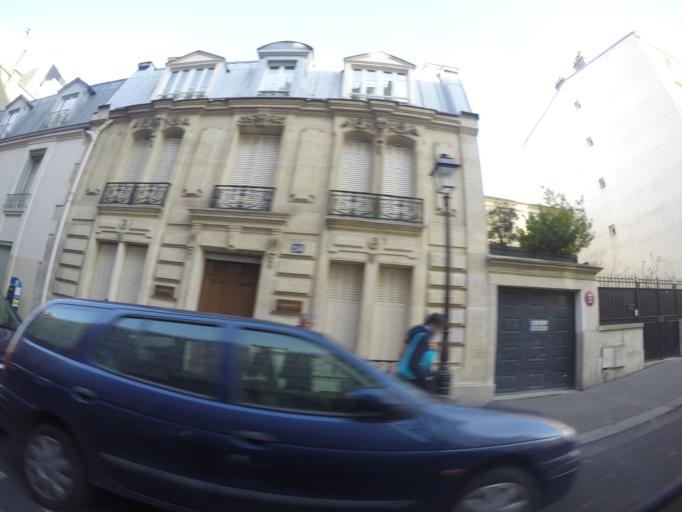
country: FR
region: Ile-de-France
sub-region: Paris
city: Saint-Ouen
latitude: 48.8885
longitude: 2.3440
